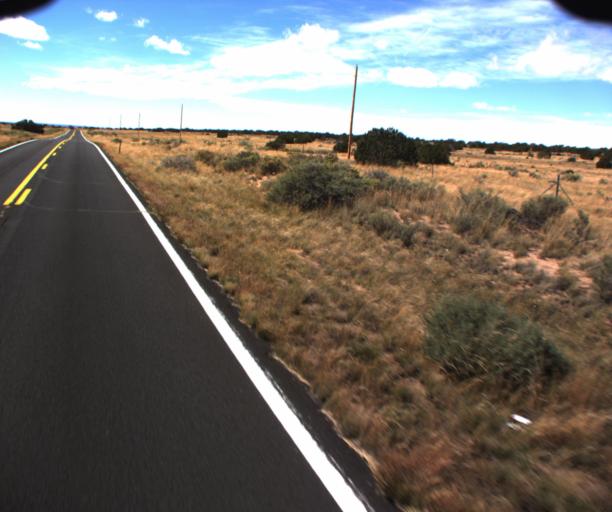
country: US
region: Arizona
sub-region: Apache County
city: Houck
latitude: 34.9328
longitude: -109.1925
